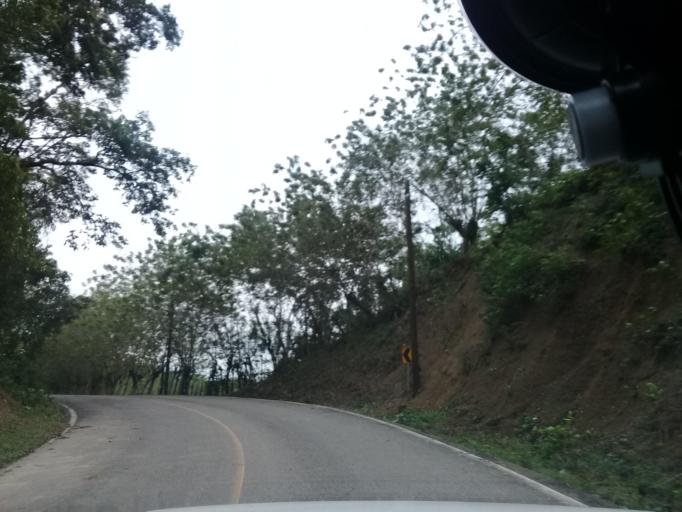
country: MX
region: Veracruz
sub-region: Chalma
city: San Pedro Coyutla
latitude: 21.2130
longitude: -98.4257
